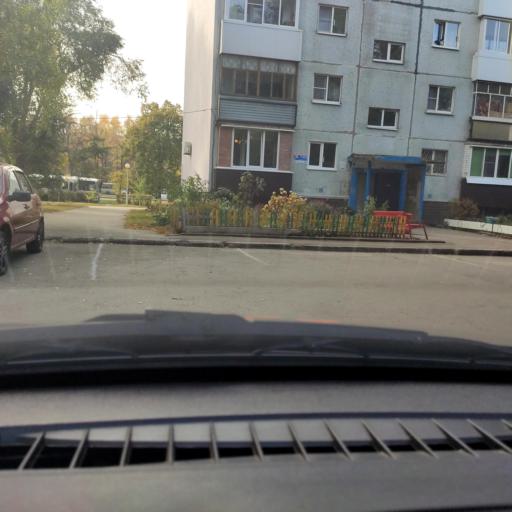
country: RU
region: Samara
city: Tol'yatti
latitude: 53.5309
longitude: 49.2688
